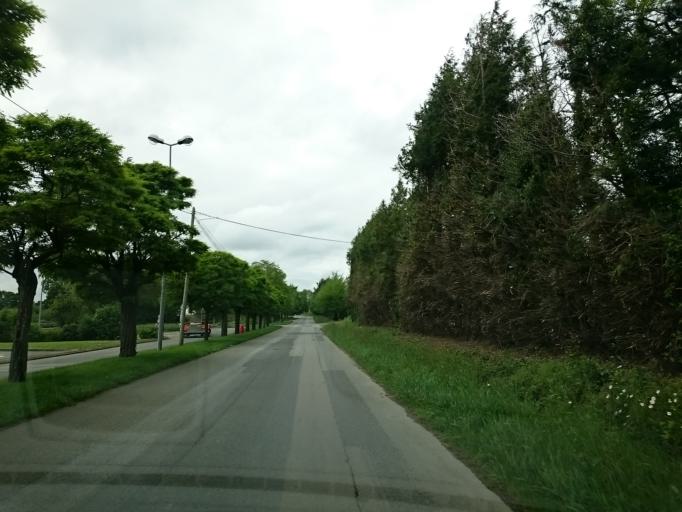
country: FR
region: Brittany
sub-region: Departement d'Ille-et-Vilaine
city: Vern-sur-Seiche
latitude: 48.0552
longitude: -1.6103
